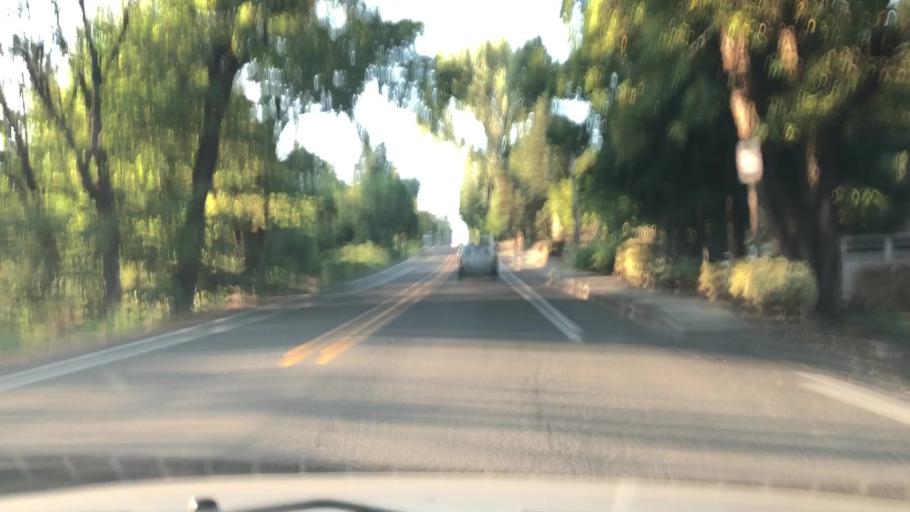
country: US
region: Oregon
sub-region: Clackamas County
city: Oak Grove
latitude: 45.4122
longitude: -122.6455
